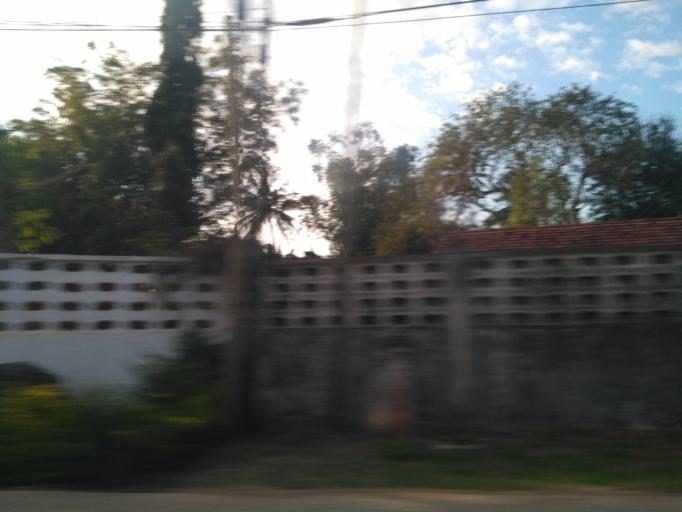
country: TZ
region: Dar es Salaam
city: Magomeni
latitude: -6.7821
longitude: 39.2712
